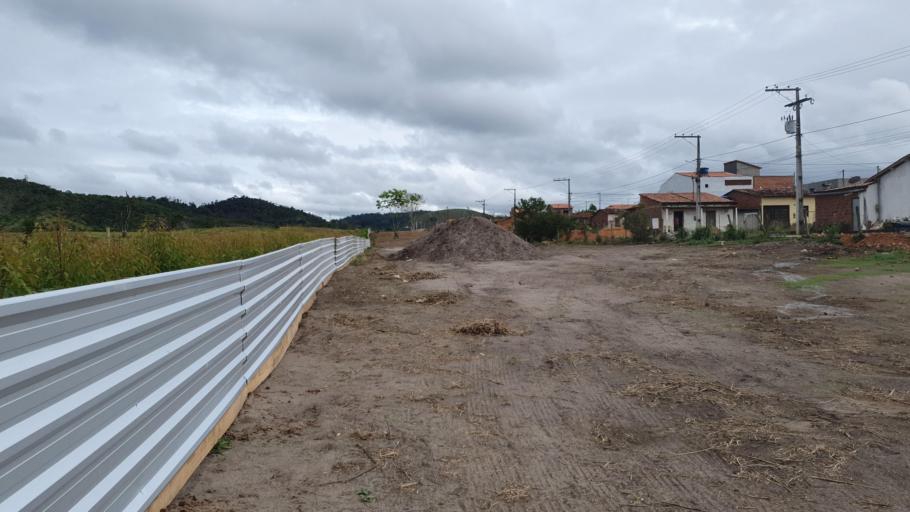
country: BR
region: Bahia
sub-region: Itagiba
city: Itagiba
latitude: -14.4260
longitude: -39.9061
